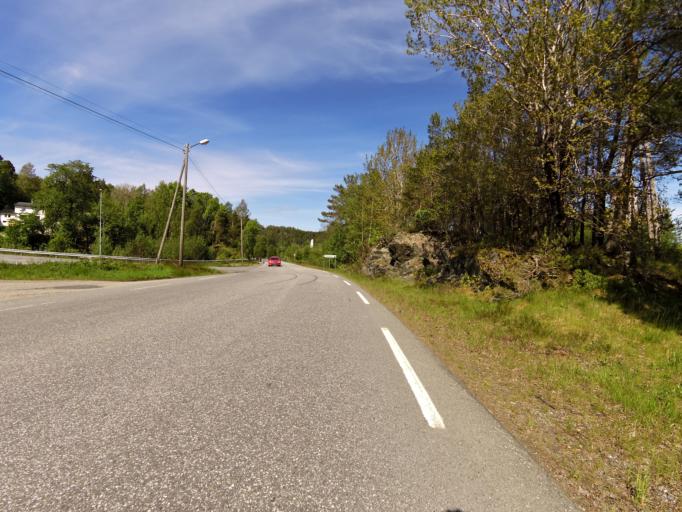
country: NO
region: Hordaland
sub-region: Stord
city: Sagvag
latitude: 59.7839
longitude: 5.4138
